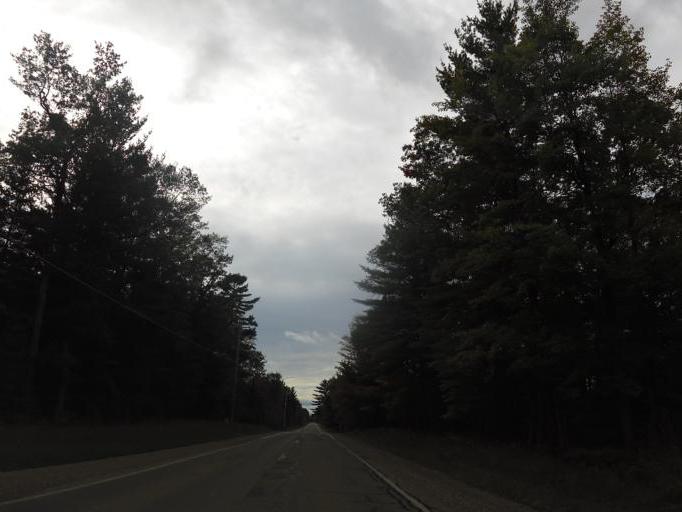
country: US
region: Michigan
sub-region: Roscommon County
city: Saint Helen
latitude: 44.3491
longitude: -84.4764
